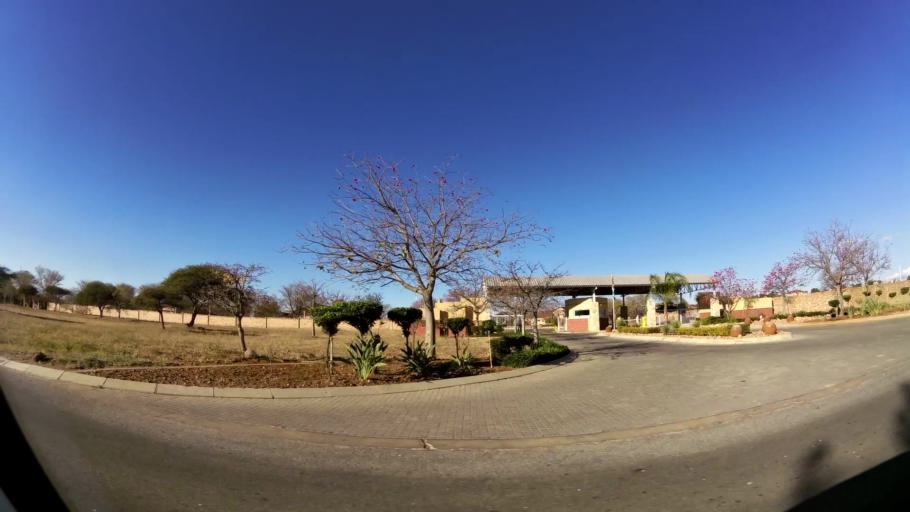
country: ZA
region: Limpopo
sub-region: Capricorn District Municipality
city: Polokwane
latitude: -23.8861
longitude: 29.4748
